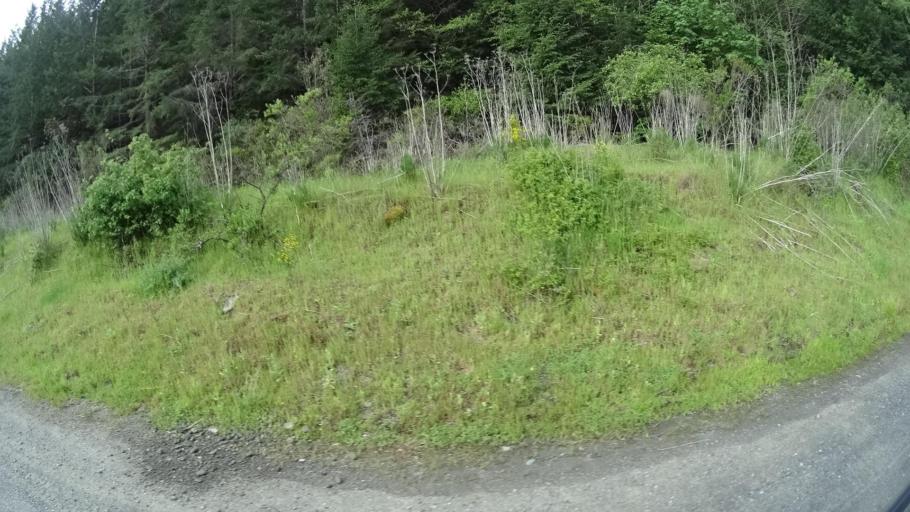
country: US
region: California
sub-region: Humboldt County
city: Redway
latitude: 40.3243
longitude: -123.8375
